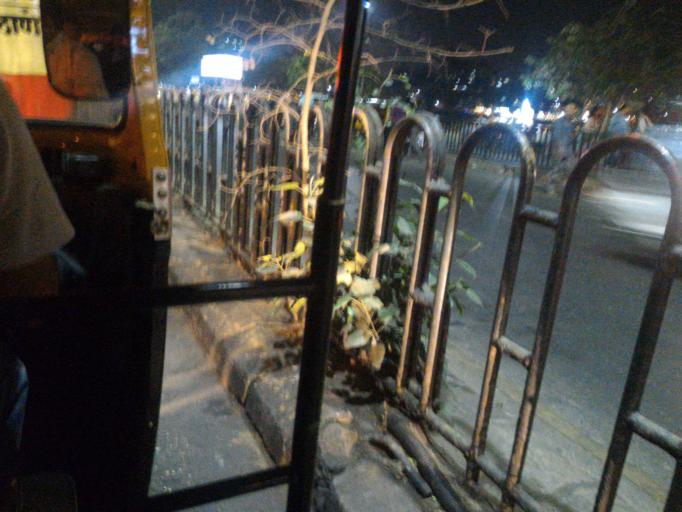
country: IN
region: Maharashtra
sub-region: Thane
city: Thane
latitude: 19.1942
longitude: 72.9769
